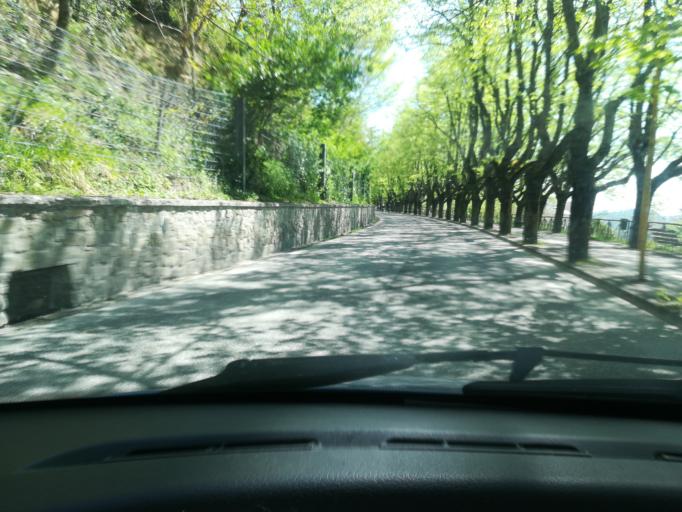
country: IT
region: The Marches
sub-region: Provincia di Macerata
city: Cingoli
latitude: 43.3730
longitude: 13.2146
